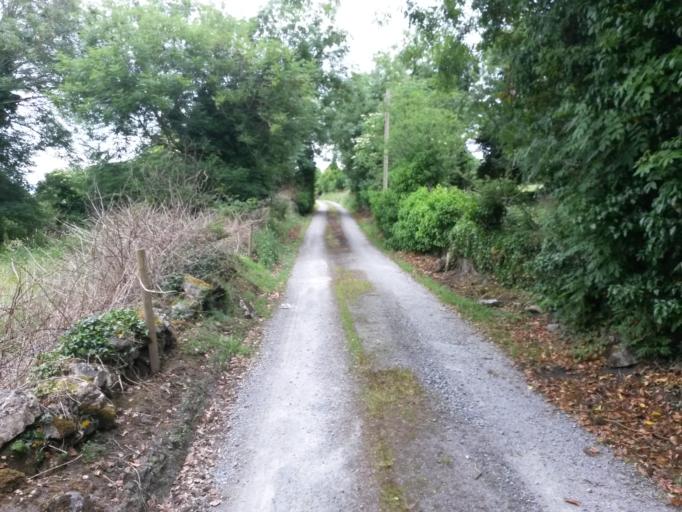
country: IE
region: Munster
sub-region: An Clar
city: Ennis
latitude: 52.9022
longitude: -9.0650
